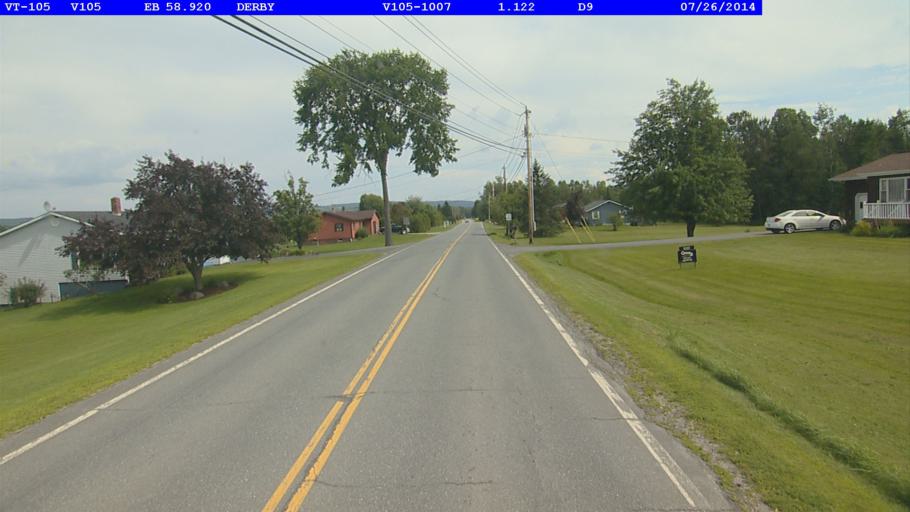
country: US
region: Vermont
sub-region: Orleans County
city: Newport
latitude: 44.9401
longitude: -72.1292
